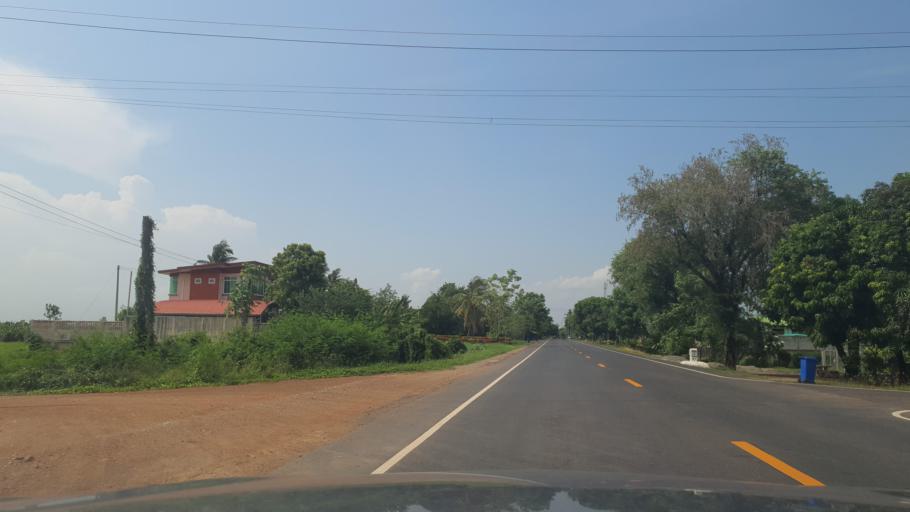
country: TH
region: Sukhothai
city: Si Samrong
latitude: 17.1539
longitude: 99.8263
